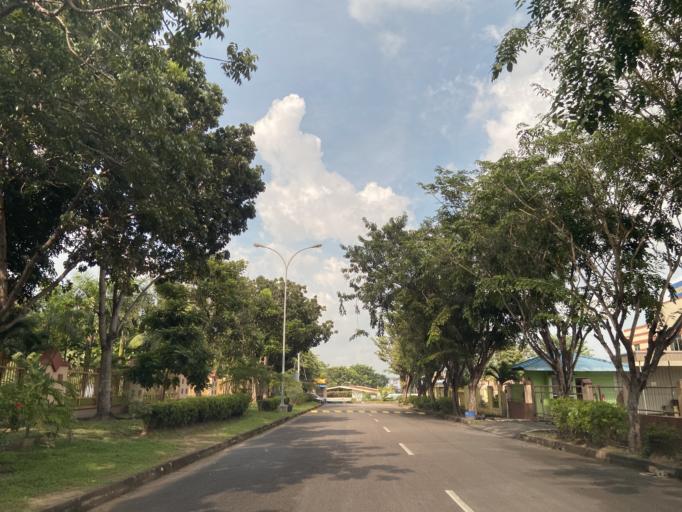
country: SG
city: Singapore
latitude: 1.1049
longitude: 104.0699
